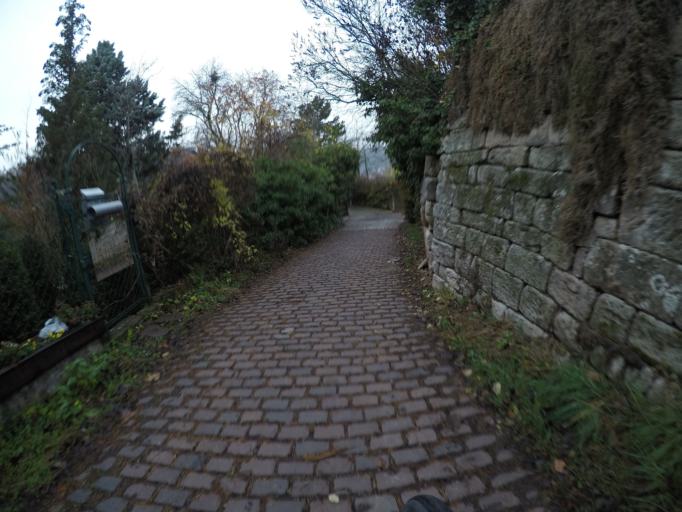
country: DE
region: Baden-Wuerttemberg
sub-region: Regierungsbezirk Stuttgart
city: Stuttgart
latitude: 48.7556
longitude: 9.1633
